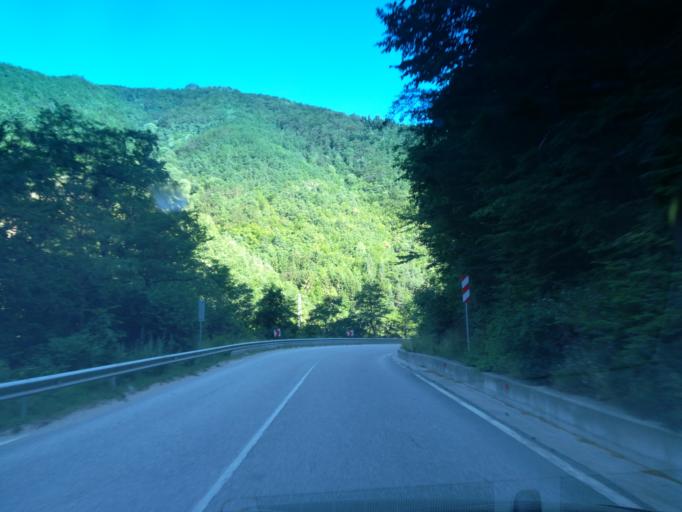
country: BG
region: Smolyan
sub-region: Obshtina Chepelare
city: Chepelare
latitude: 41.7955
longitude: 24.7100
